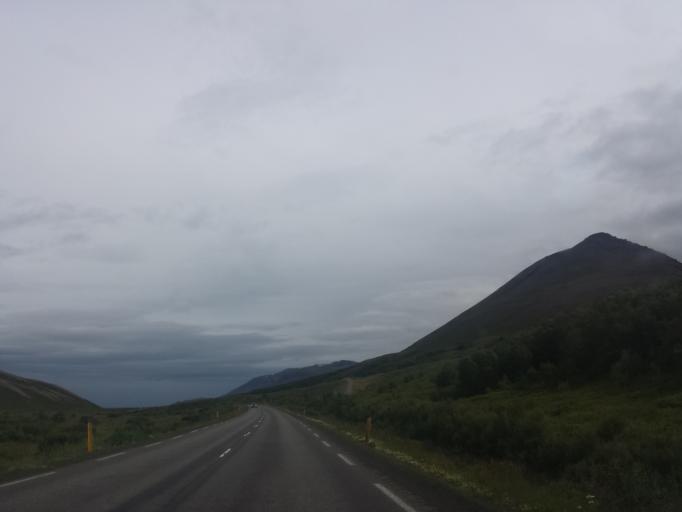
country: IS
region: Northeast
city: Akureyri
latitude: 65.7419
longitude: -17.8724
